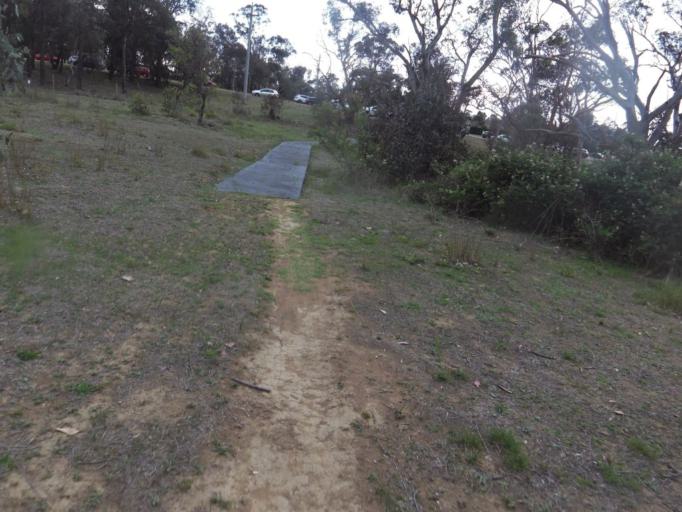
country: AU
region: Australian Capital Territory
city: Forrest
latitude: -35.3450
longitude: 149.1377
